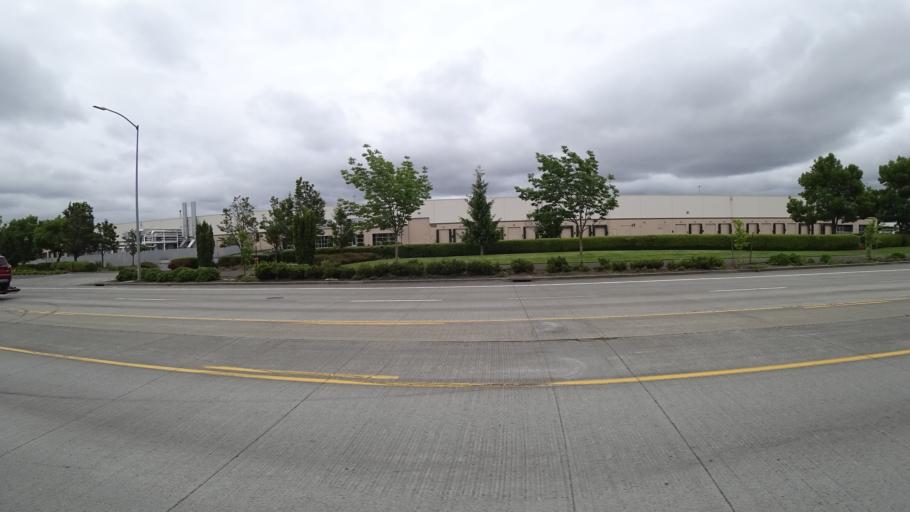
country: US
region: Washington
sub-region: Clark County
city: Vancouver
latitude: 45.6275
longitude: -122.7400
